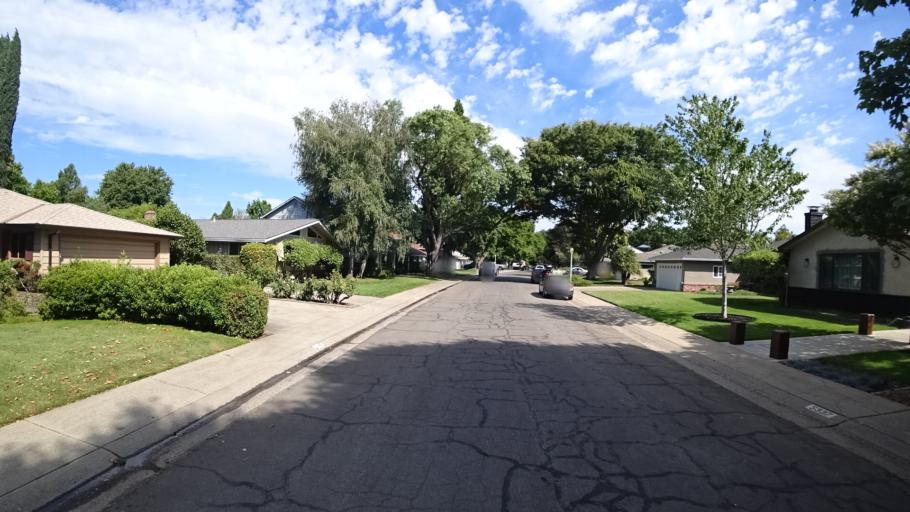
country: US
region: California
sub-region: Sacramento County
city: Arden-Arcade
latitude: 38.5790
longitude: -121.4296
